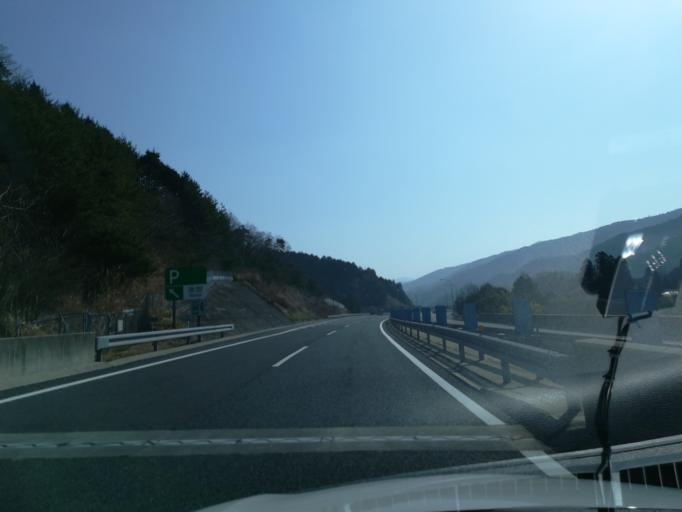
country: JP
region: Tokushima
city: Ikedacho
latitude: 34.0059
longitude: 133.7028
